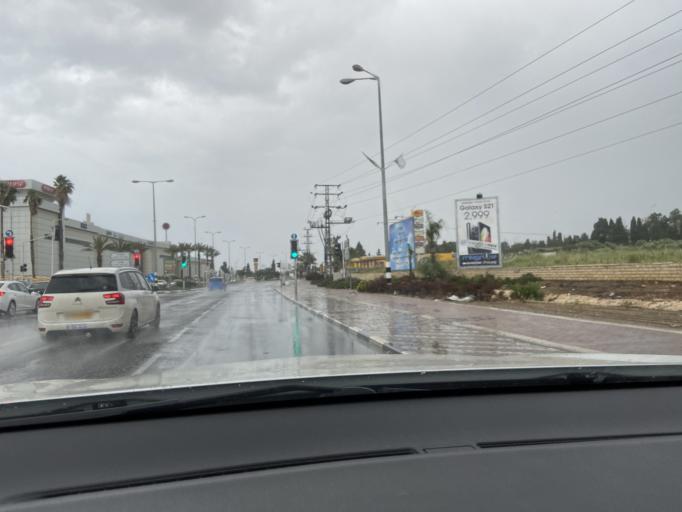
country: IL
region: Northern District
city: El Mazra`a
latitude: 32.9886
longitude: 35.0956
